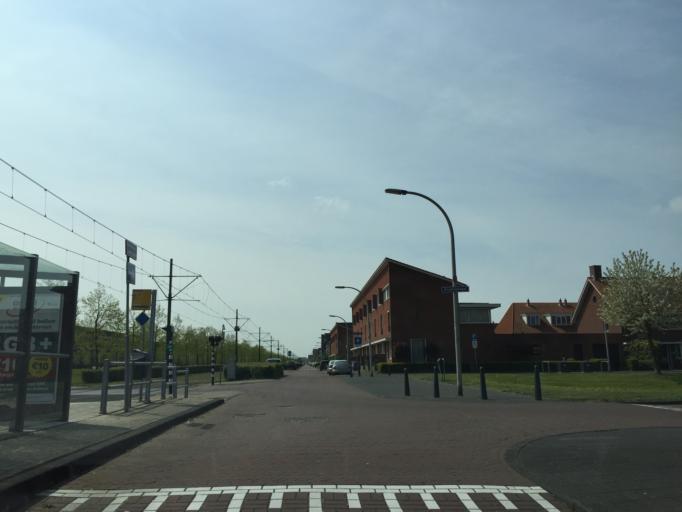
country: NL
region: South Holland
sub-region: Gemeente Den Haag
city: Ypenburg
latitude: 52.0486
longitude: 4.3826
